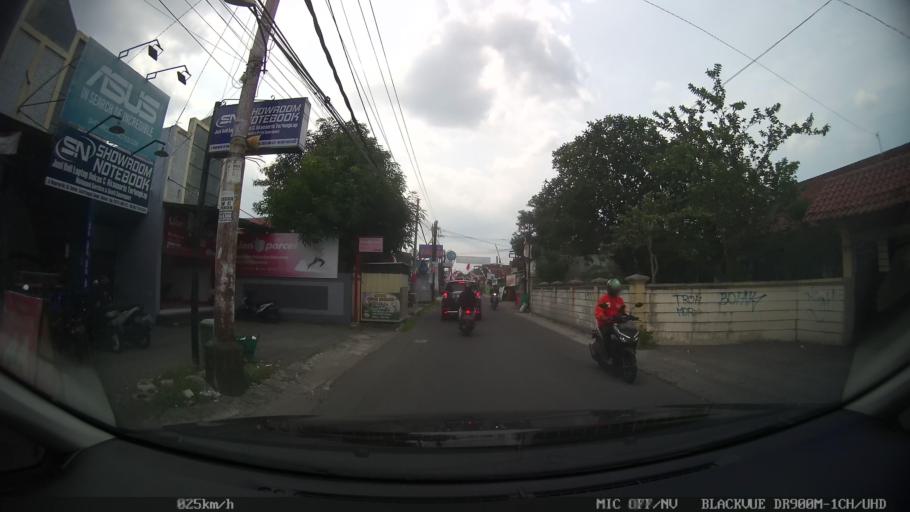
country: ID
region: Daerah Istimewa Yogyakarta
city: Yogyakarta
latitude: -7.7851
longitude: 110.3997
